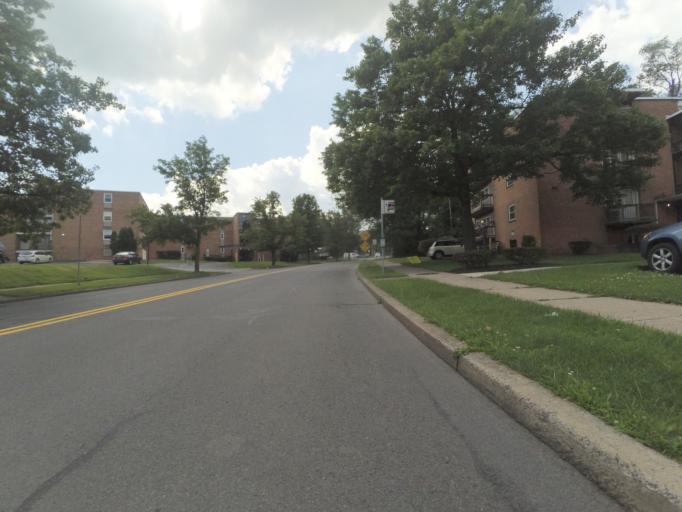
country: US
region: Pennsylvania
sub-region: Centre County
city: State College
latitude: 40.7857
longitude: -77.8489
